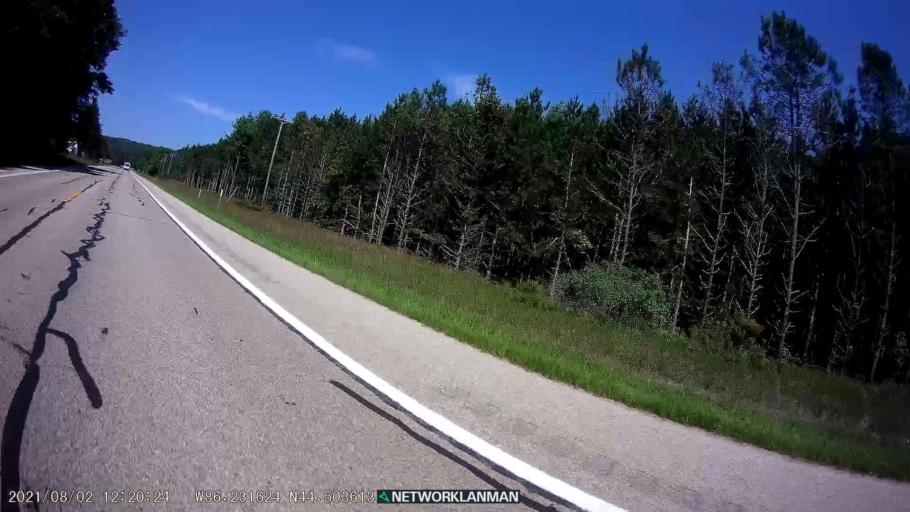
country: US
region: Michigan
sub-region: Benzie County
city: Frankfort
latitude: 44.5041
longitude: -86.2316
